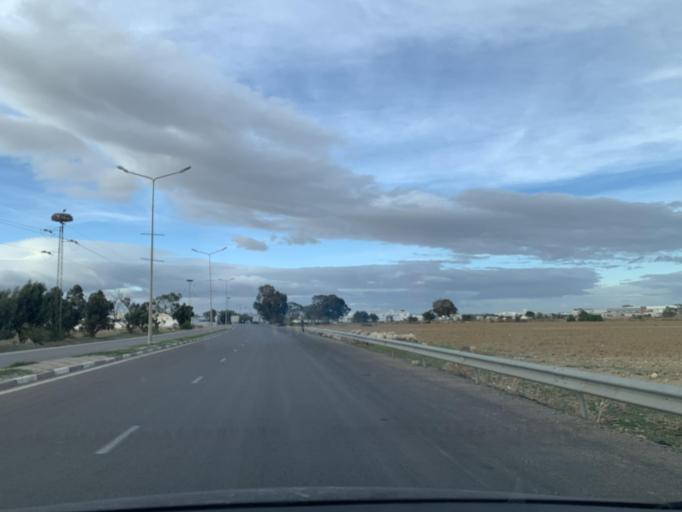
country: TN
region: Susah
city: Harqalah
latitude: 36.1026
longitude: 10.3886
